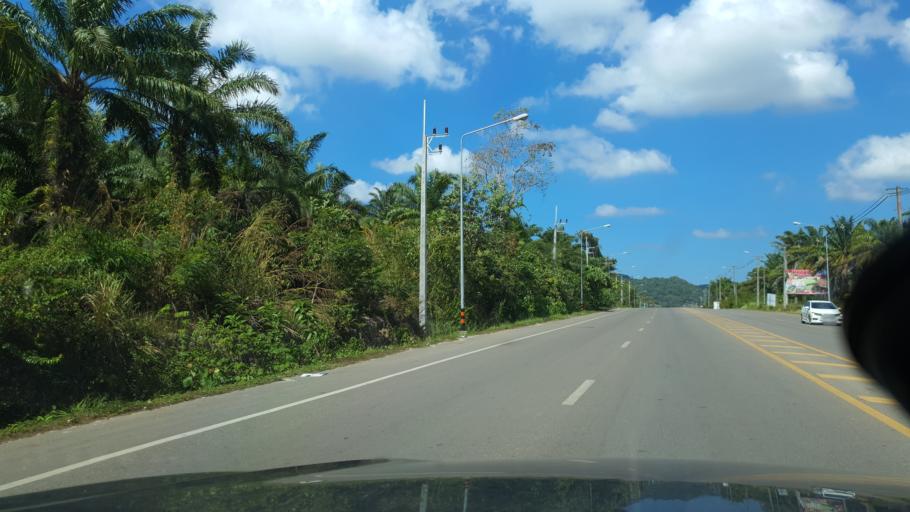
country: TH
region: Phangnga
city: Ban Ao Nang
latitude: 8.0369
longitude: 98.8550
